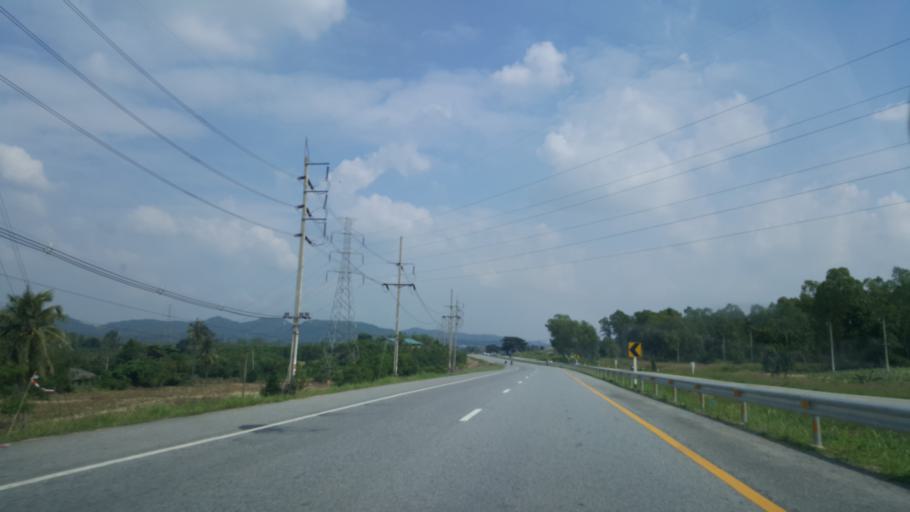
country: TH
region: Chon Buri
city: Ban Talat Bueng
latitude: 12.9281
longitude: 101.0351
